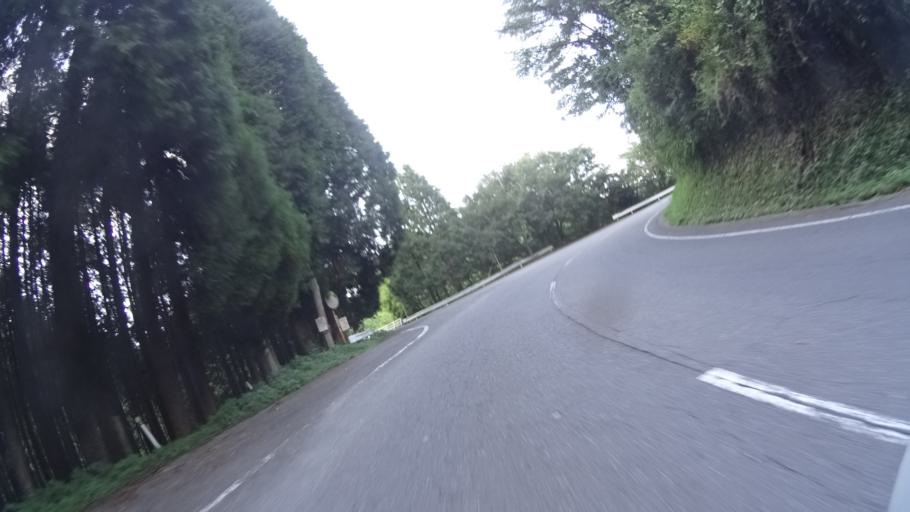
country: JP
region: Kumamoto
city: Ozu
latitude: 32.6880
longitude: 131.0109
